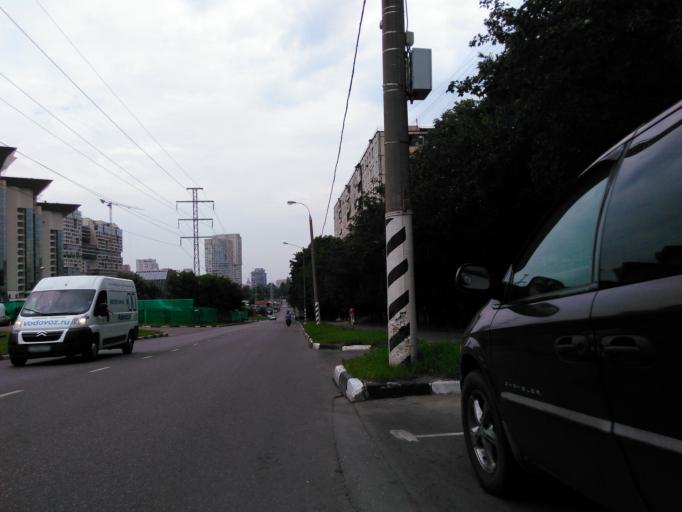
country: RU
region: Moskovskaya
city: Semenovskoye
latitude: 55.6770
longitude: 37.5501
